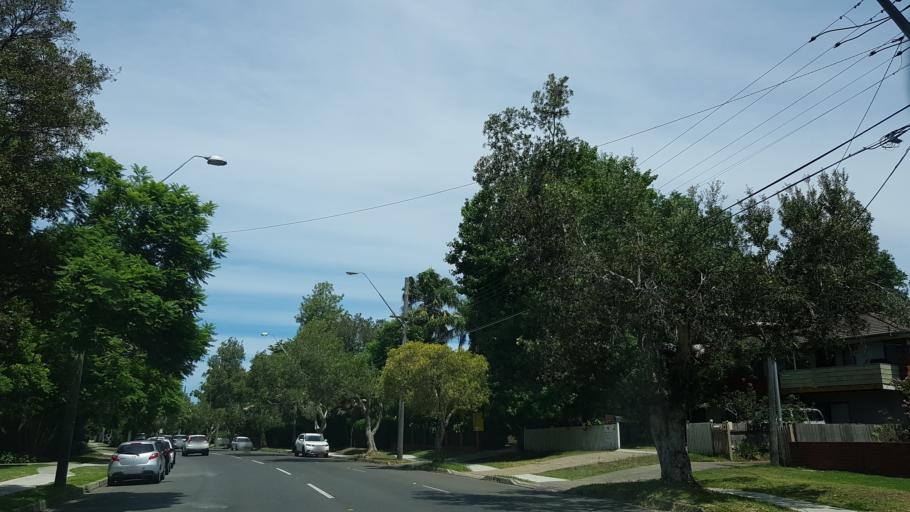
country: AU
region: New South Wales
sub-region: Pittwater
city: Bay View
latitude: -33.6710
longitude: 151.3023
